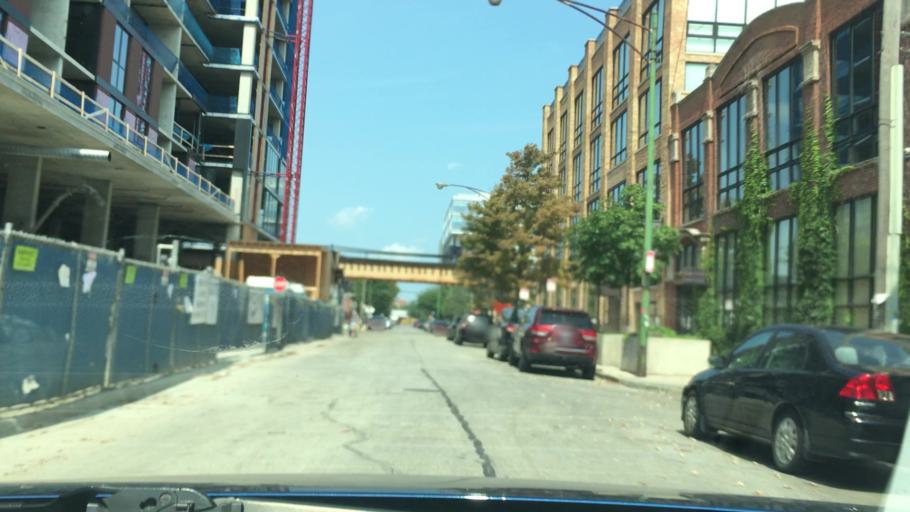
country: US
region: Illinois
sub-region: Cook County
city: Chicago
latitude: 41.8847
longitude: -87.6607
